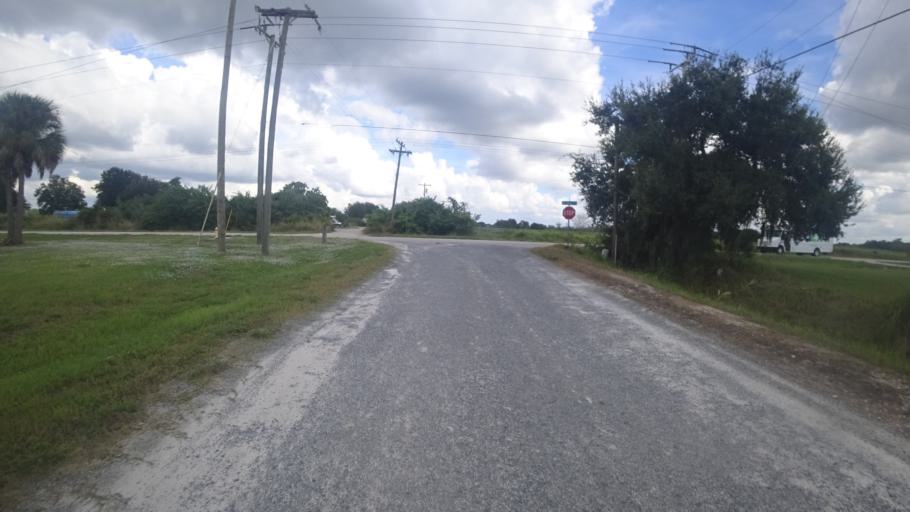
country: US
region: Florida
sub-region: Manatee County
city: Memphis
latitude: 27.6161
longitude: -82.5277
